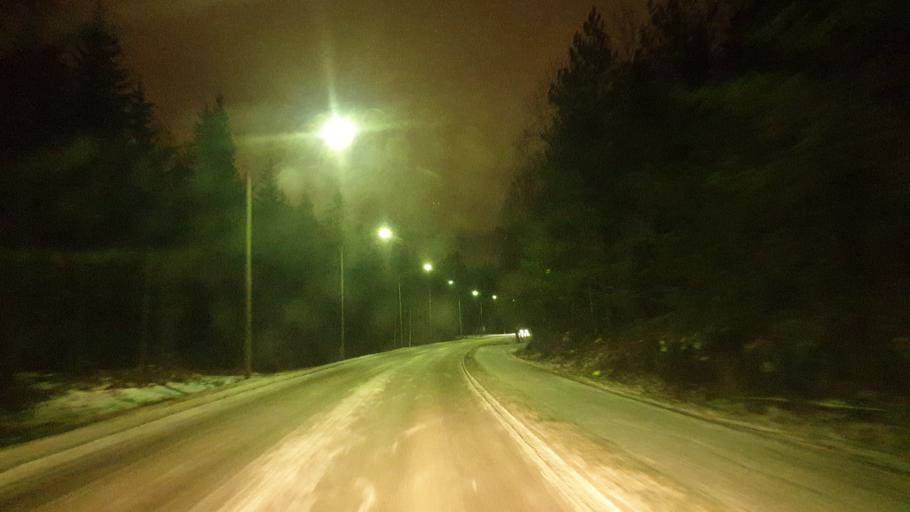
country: FI
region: Southern Savonia
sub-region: Savonlinna
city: Savonlinna
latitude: 61.8606
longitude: 28.9470
